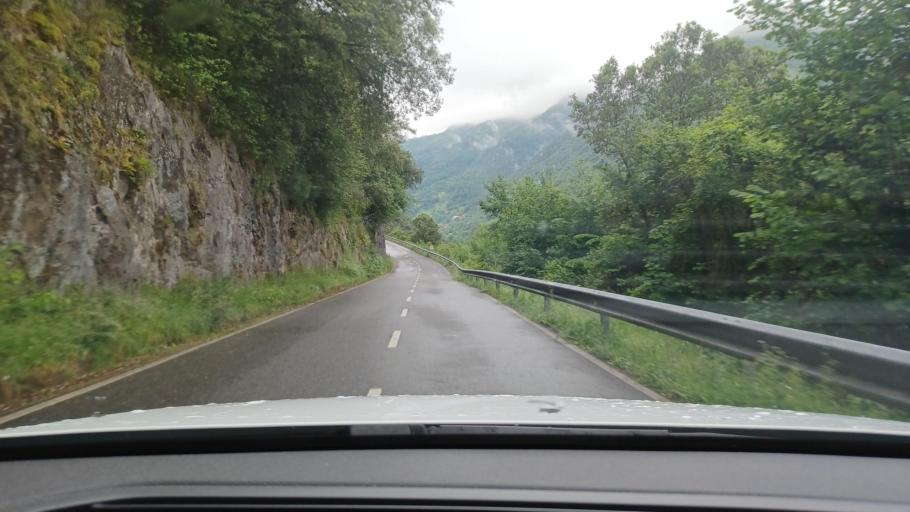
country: ES
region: Asturias
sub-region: Province of Asturias
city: Proaza
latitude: 43.2844
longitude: -5.9828
